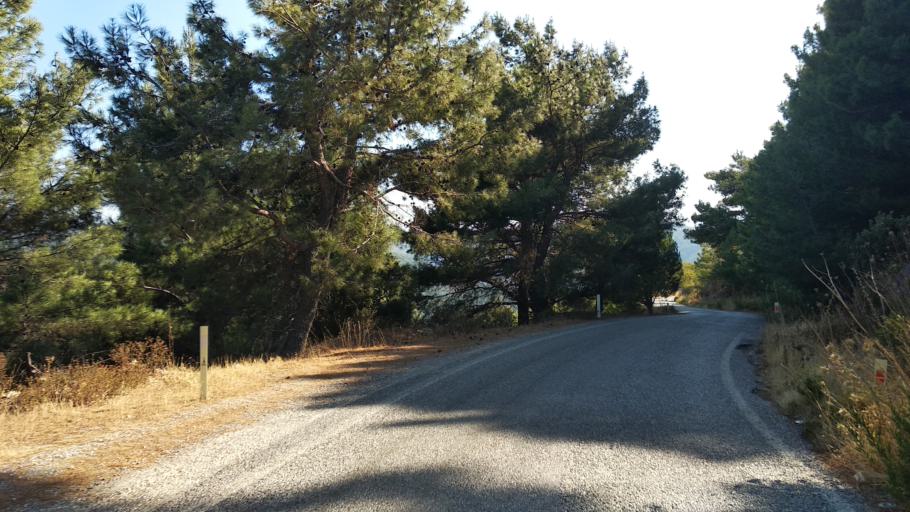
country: TR
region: Izmir
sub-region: Seferihisar
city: Seferhisar
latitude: 38.3264
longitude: 26.9423
